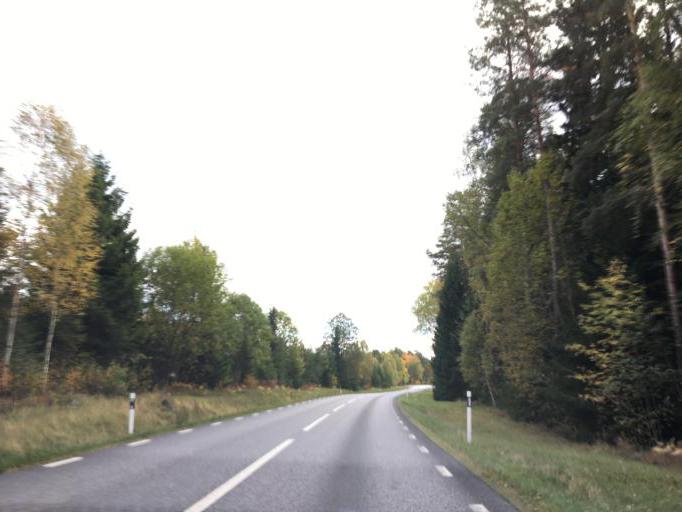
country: SE
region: Soedermanland
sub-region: Flens Kommun
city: Flen
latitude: 58.9208
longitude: 16.4232
